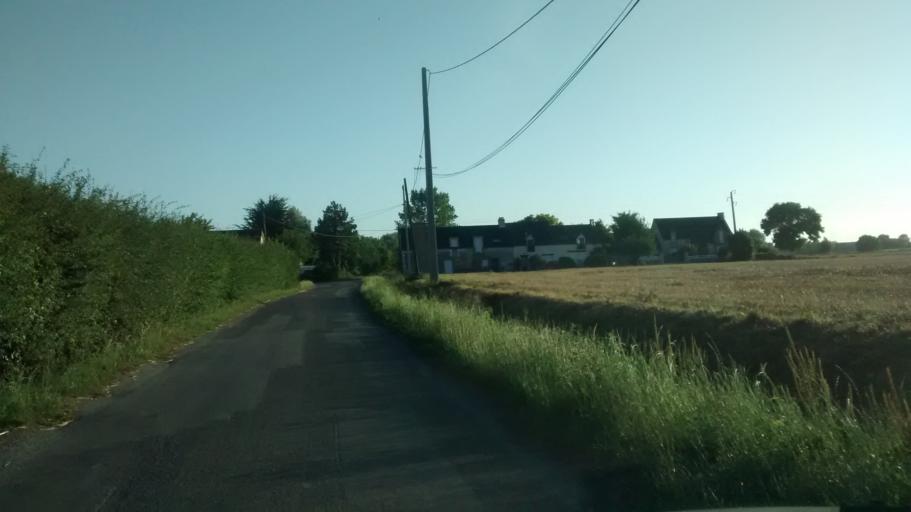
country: FR
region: Brittany
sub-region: Departement d'Ille-et-Vilaine
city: La Fresnais
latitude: 48.5998
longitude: -1.8537
